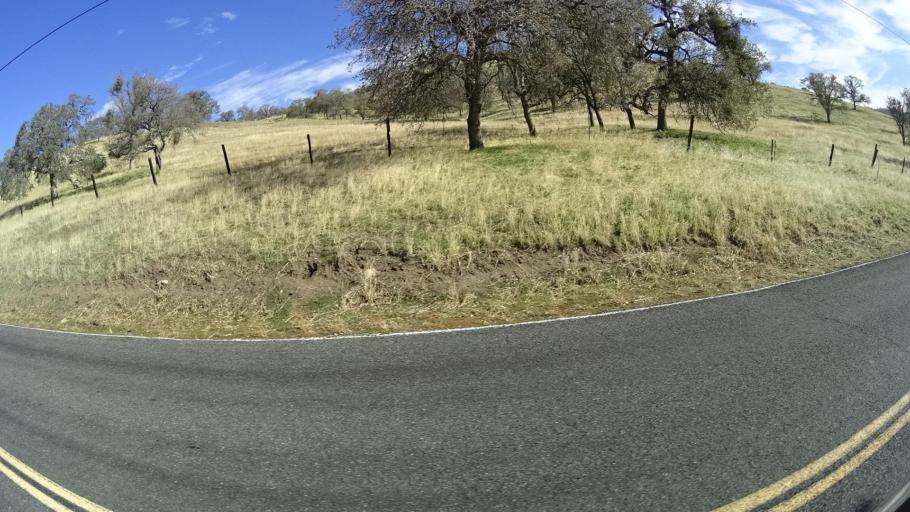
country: US
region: California
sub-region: Kern County
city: Alta Sierra
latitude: 35.6337
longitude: -118.8009
